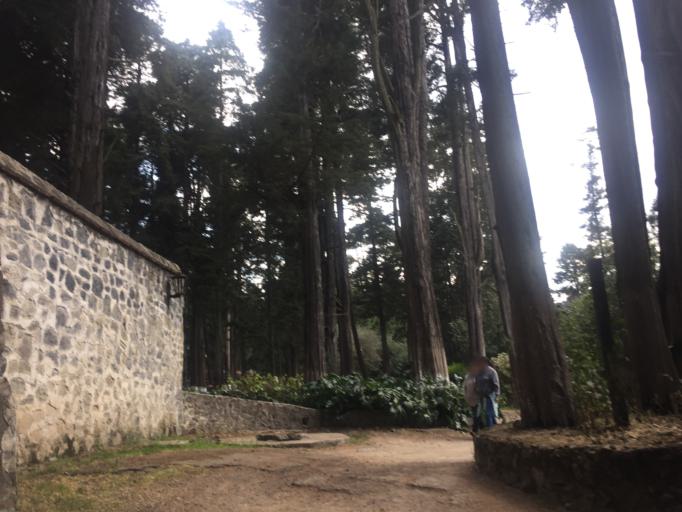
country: MX
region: Mexico City
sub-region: Cuajimalpa de Morelos
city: San Lorenzo Acopilco
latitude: 19.3148
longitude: -99.3103
